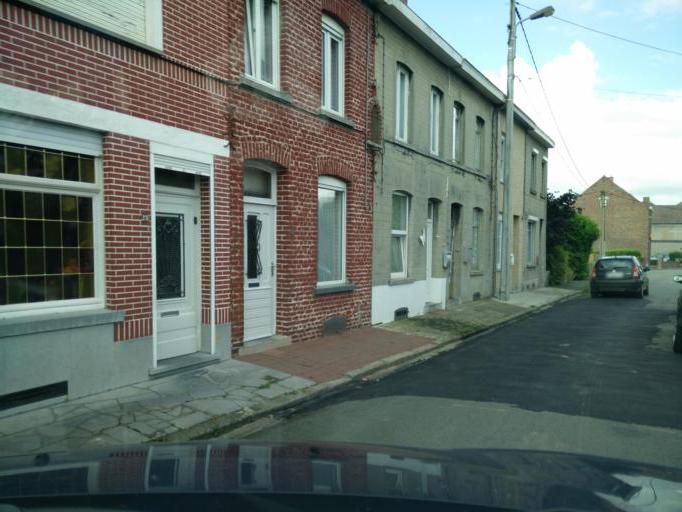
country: BE
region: Wallonia
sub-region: Province du Hainaut
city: Lessines
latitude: 50.7021
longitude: 3.8311
